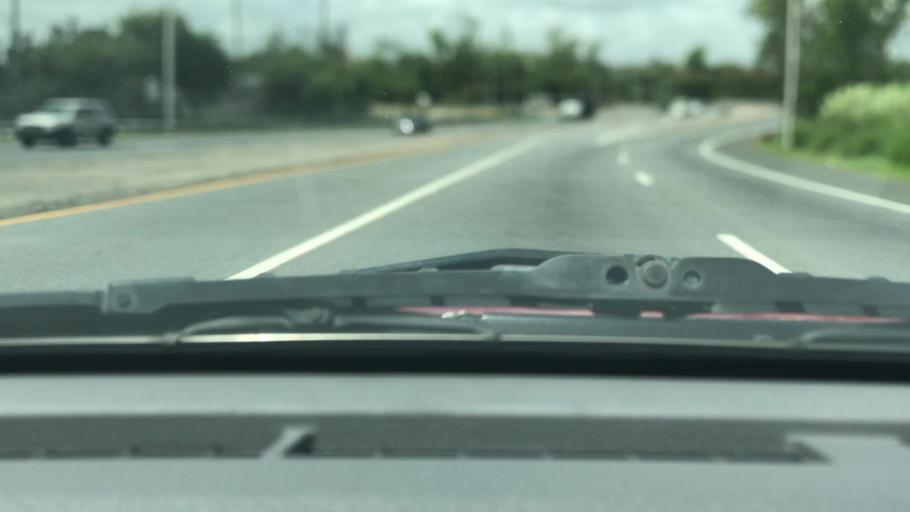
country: PR
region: Bayamon
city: Bayamon
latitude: 18.3673
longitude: -66.1670
